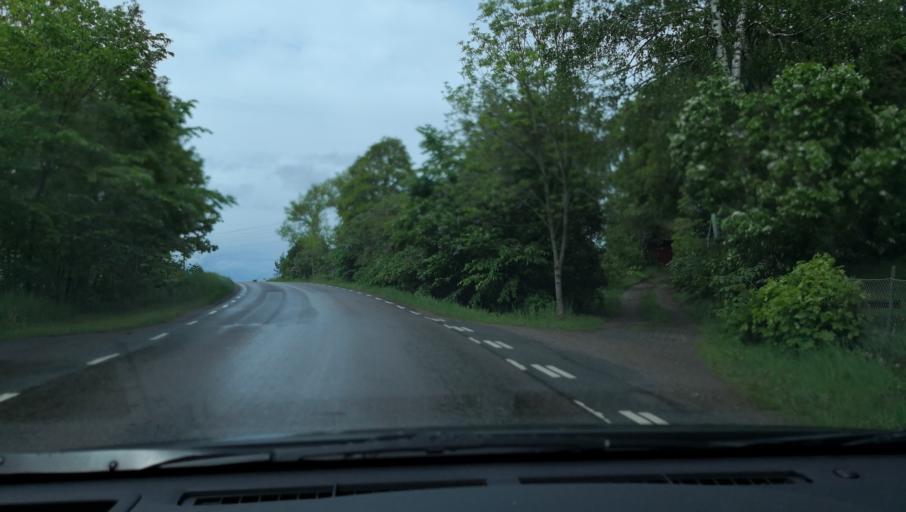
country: SE
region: Uppsala
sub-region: Enkopings Kommun
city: Orsundsbro
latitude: 59.6906
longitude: 17.3763
